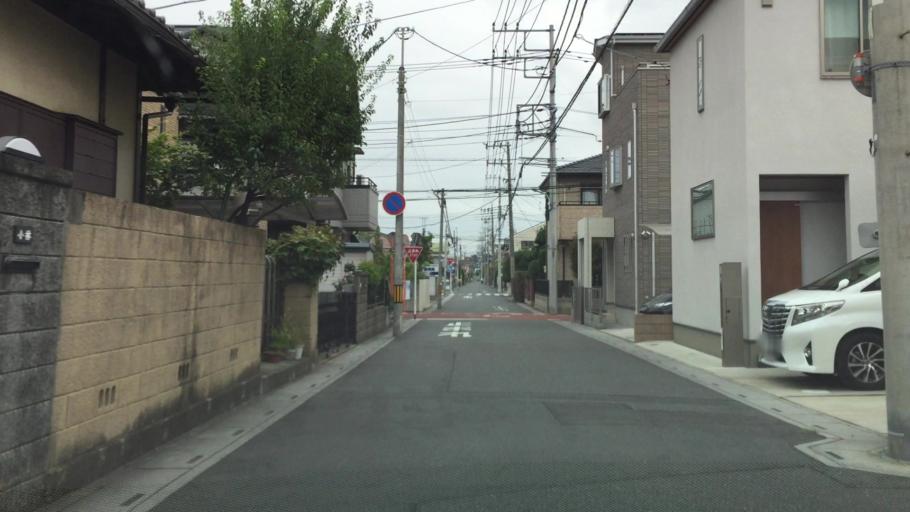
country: JP
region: Saitama
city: Ageoshimo
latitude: 35.9378
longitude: 139.6232
